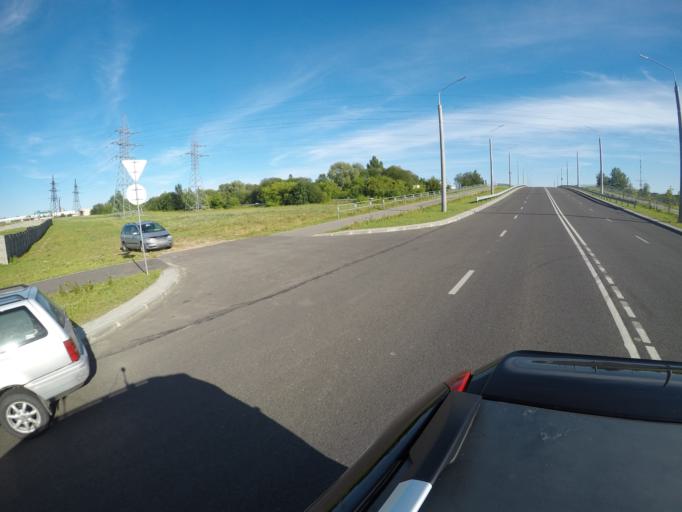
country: BY
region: Grodnenskaya
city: Hrodna
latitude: 53.7182
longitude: 23.8239
